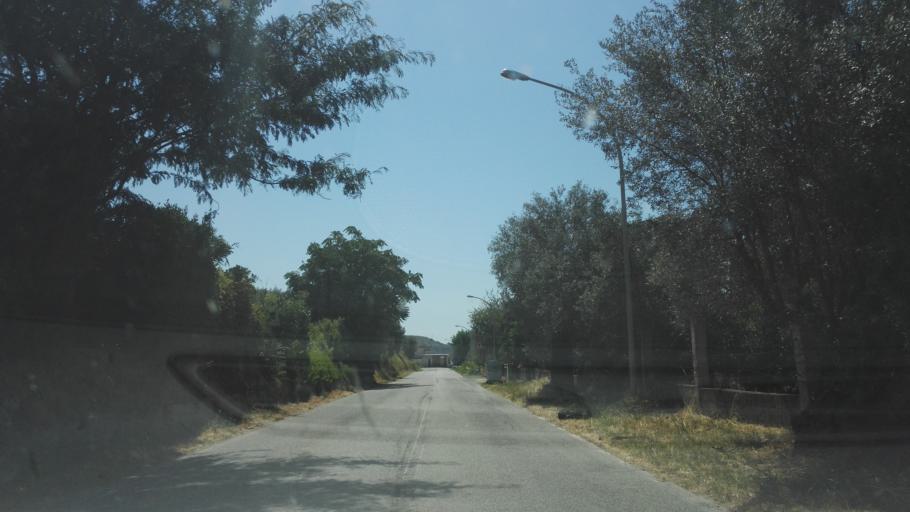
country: IT
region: Calabria
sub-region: Provincia di Catanzaro
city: Guardavalle
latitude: 38.4660
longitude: 16.5092
